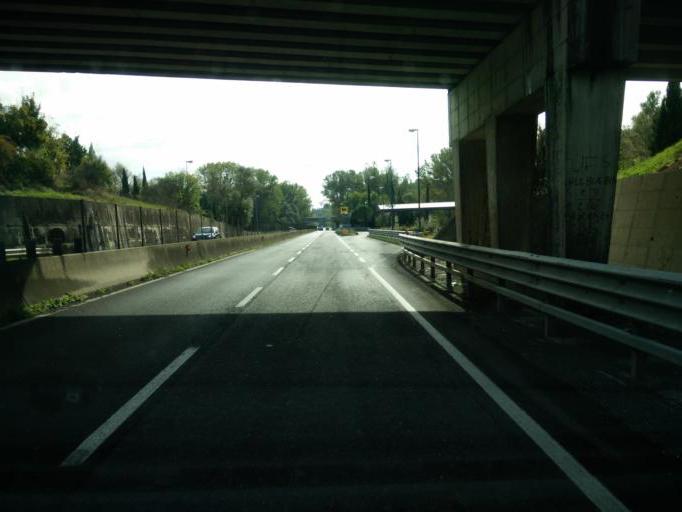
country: IT
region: Tuscany
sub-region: Provincia di Siena
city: Siena
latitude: 43.3113
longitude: 11.3114
